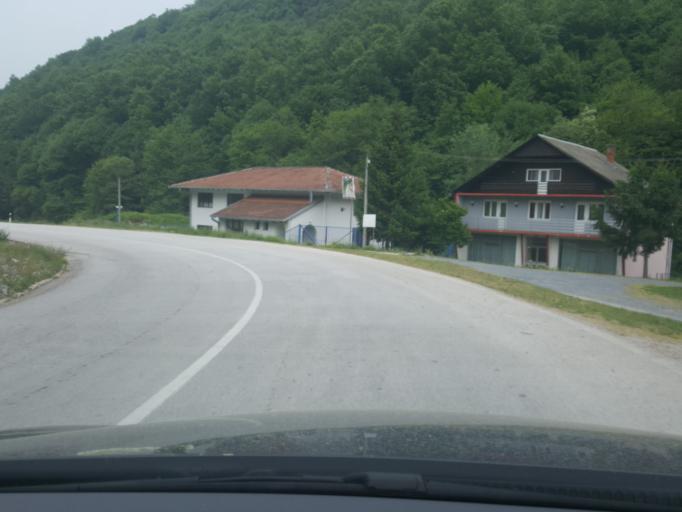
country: RS
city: Gornja Bukovica
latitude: 44.2528
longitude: 19.7960
